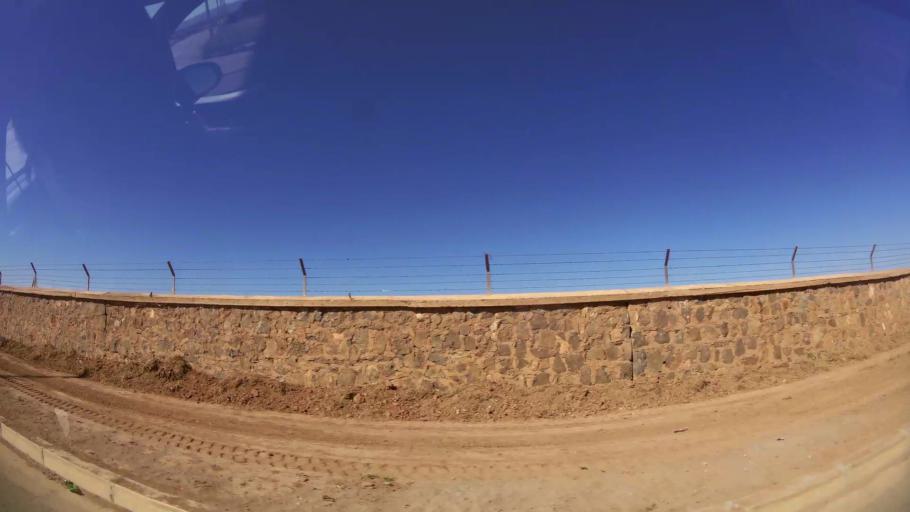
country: MA
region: Oriental
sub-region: Oujda-Angad
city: Oujda
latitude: 34.7752
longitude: -1.9317
